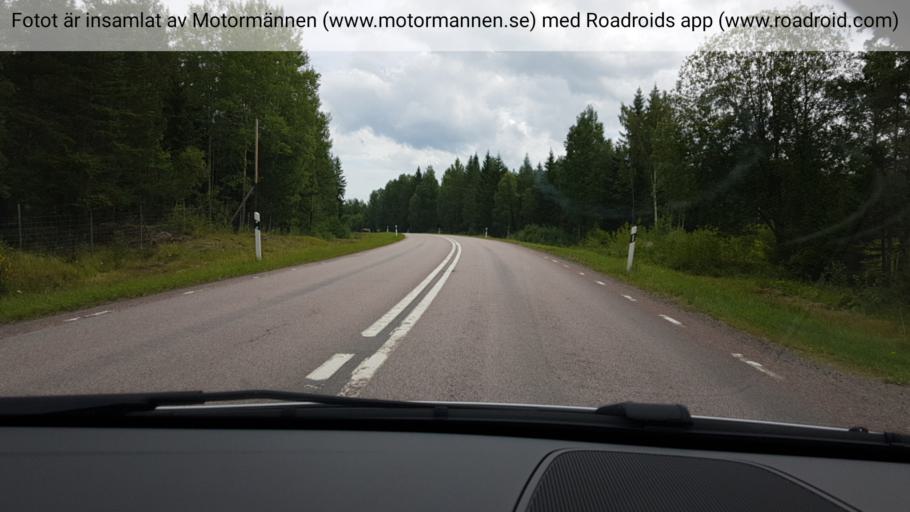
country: SE
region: Uppsala
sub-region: Osthammars Kommun
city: OEsthammar
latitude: 60.2411
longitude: 18.3176
